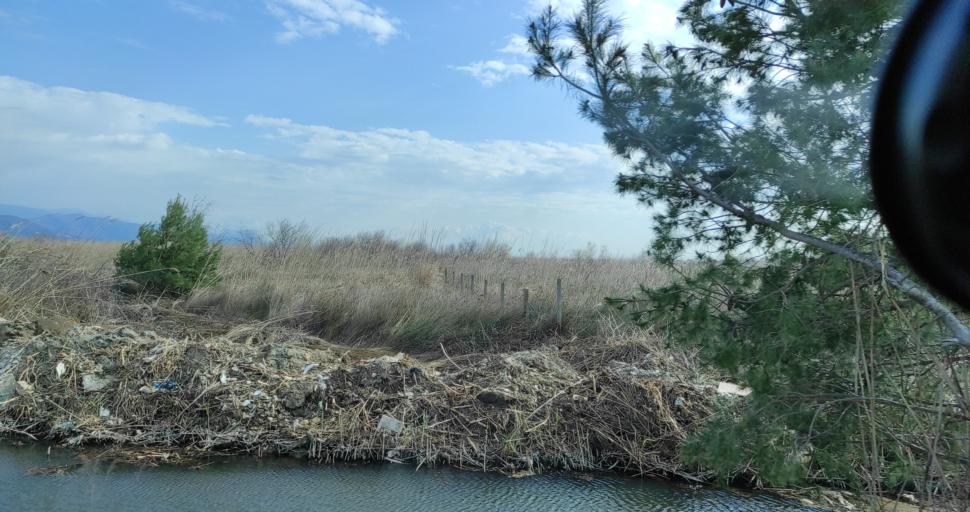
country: AL
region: Lezhe
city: Shengjin
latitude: 41.7965
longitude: 19.6084
